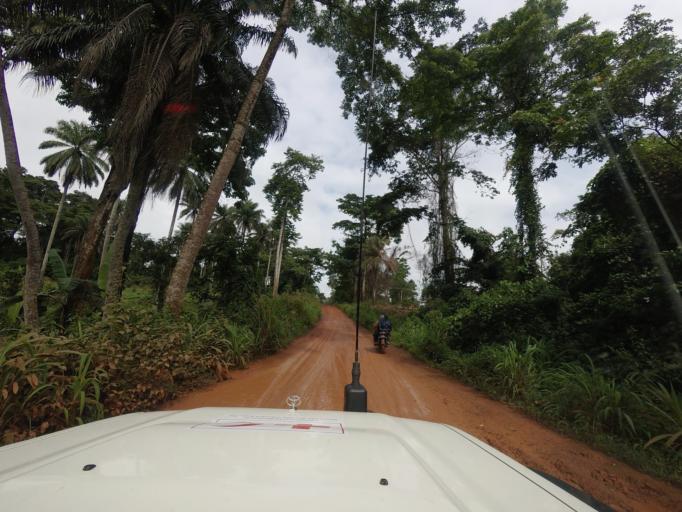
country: GN
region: Nzerekore
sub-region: Nzerekore Prefecture
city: Nzerekore
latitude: 7.7235
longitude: -8.8801
